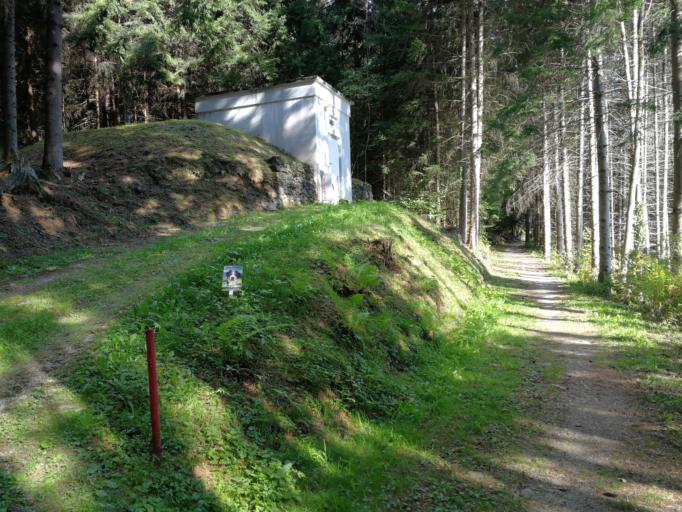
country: AT
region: Carinthia
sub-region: Politischer Bezirk Spittal an der Drau
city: Millstatt
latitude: 46.8101
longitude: 13.5644
